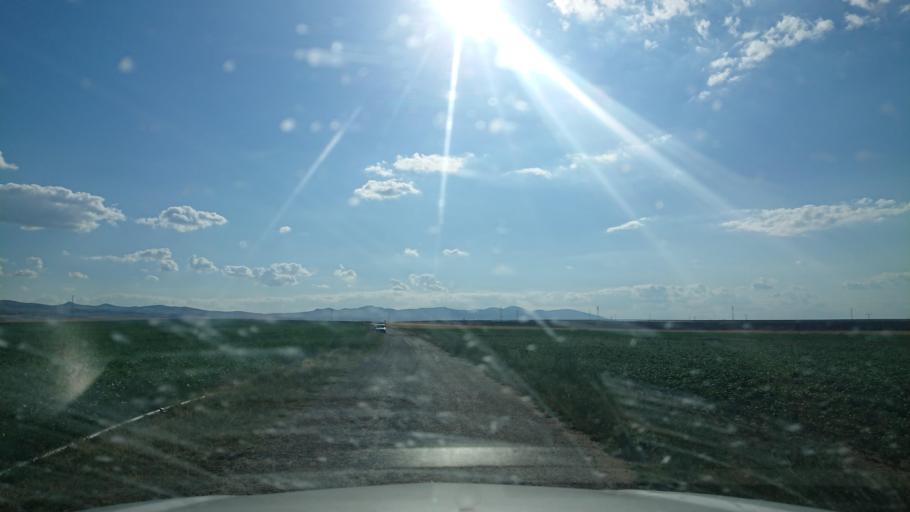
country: TR
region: Aksaray
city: Sariyahsi
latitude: 39.0200
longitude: 33.8862
